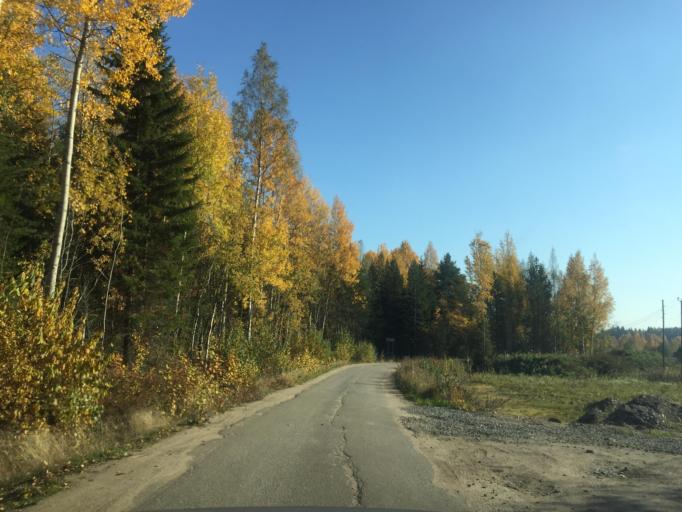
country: RU
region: Leningrad
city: Priozersk
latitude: 61.2895
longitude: 30.0839
